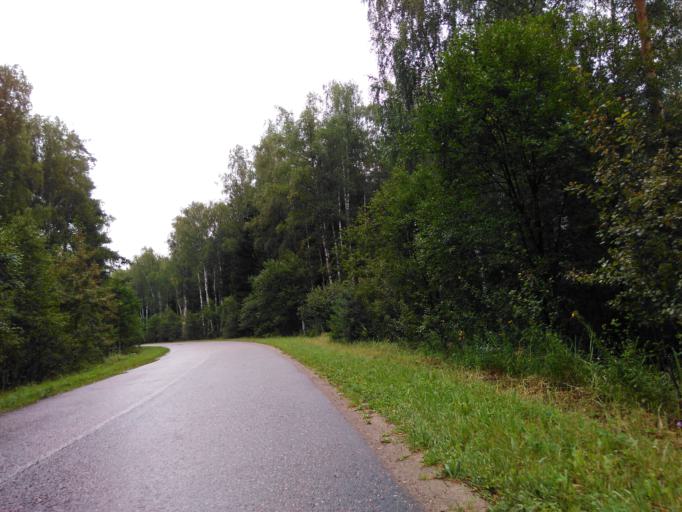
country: RU
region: Moskovskaya
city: Elektrogorsk
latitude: 55.9432
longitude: 38.6538
